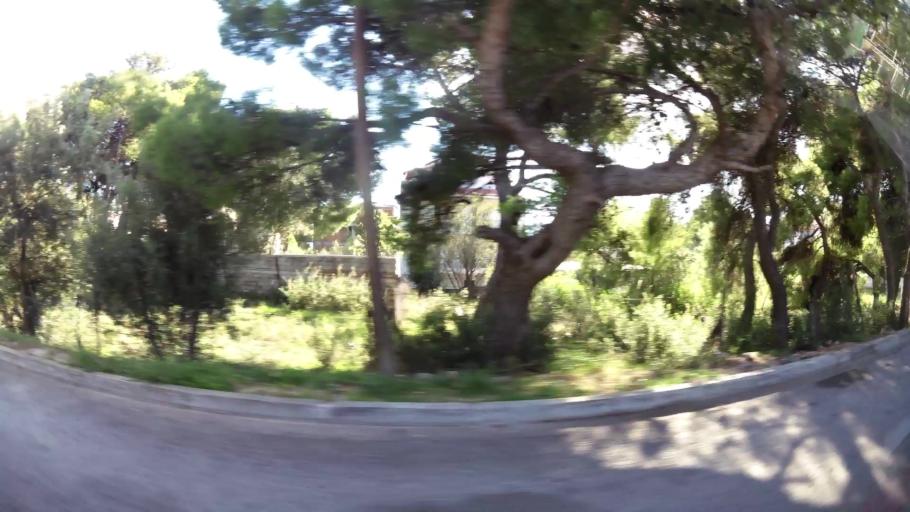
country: GR
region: Attica
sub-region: Nomarchia Anatolikis Attikis
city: Anthousa
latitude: 38.0305
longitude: 23.8771
